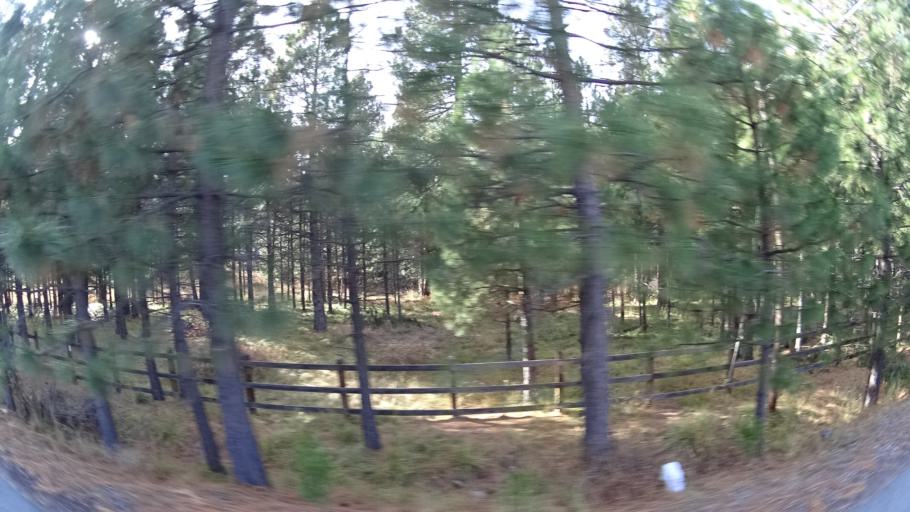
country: US
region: California
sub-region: Siskiyou County
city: Weed
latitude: 41.3866
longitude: -122.4093
